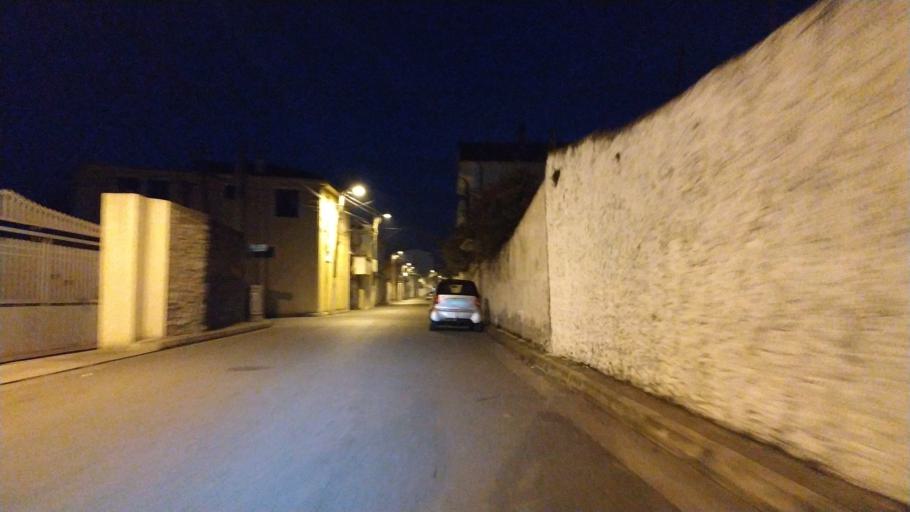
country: AL
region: Shkoder
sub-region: Rrethi i Shkodres
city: Shkoder
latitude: 42.0648
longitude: 19.5057
